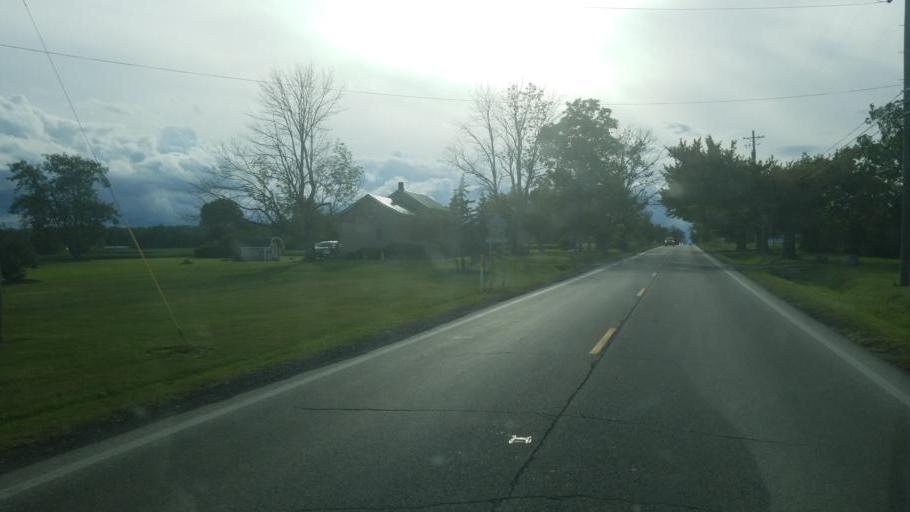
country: US
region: Ohio
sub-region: Geauga County
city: Middlefield
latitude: 41.4588
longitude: -81.0066
